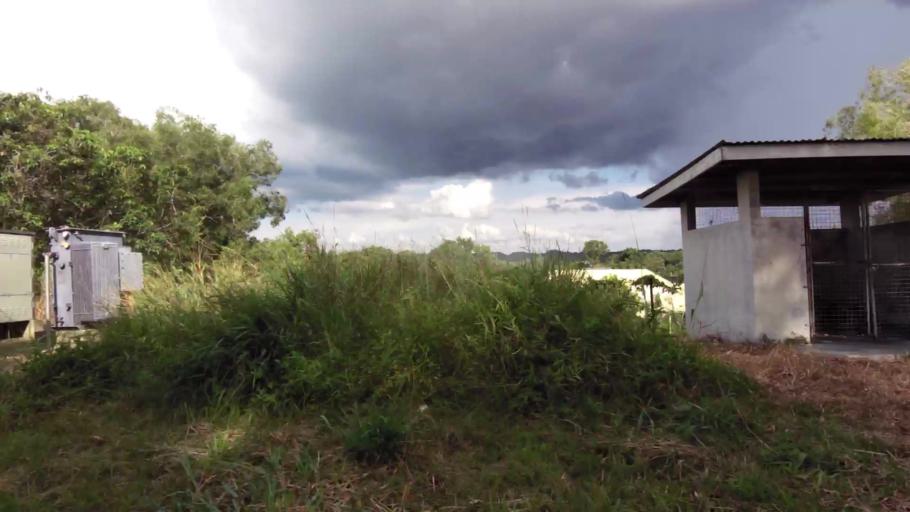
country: BN
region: Brunei and Muara
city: Bandar Seri Begawan
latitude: 4.9619
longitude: 114.9632
